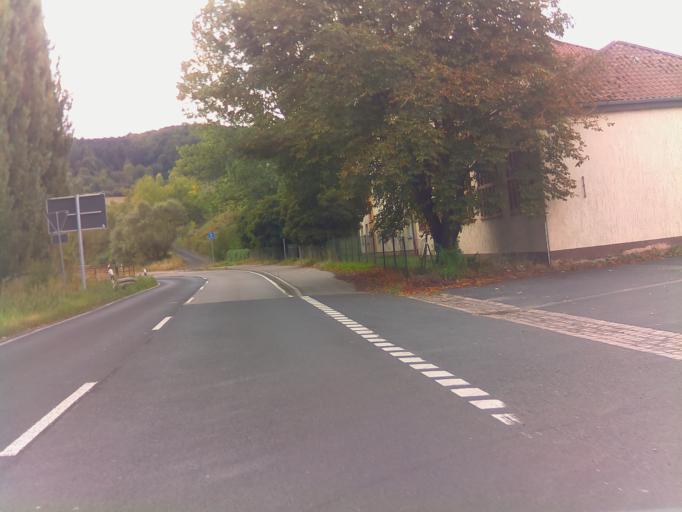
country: DE
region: Thuringia
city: Ritschenhausen
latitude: 50.5198
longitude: 10.4304
